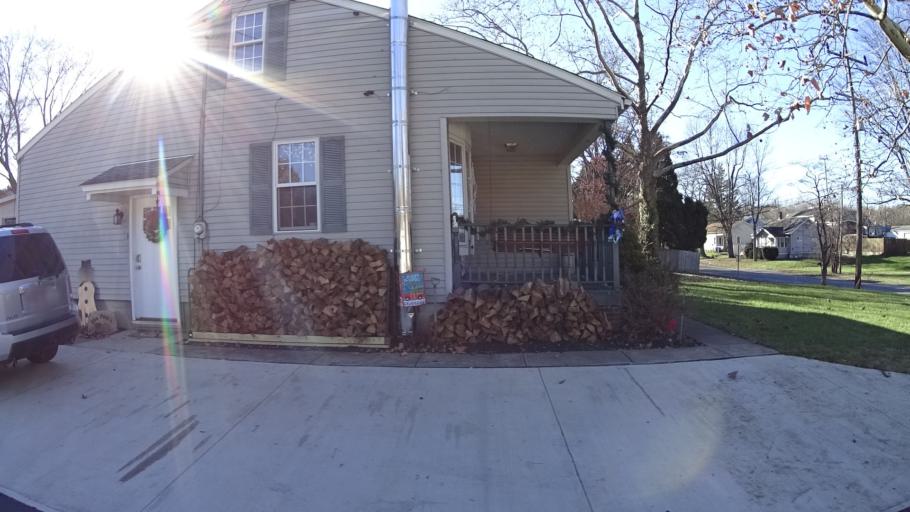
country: US
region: Ohio
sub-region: Lorain County
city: Elyria
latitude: 41.3468
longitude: -82.0959
